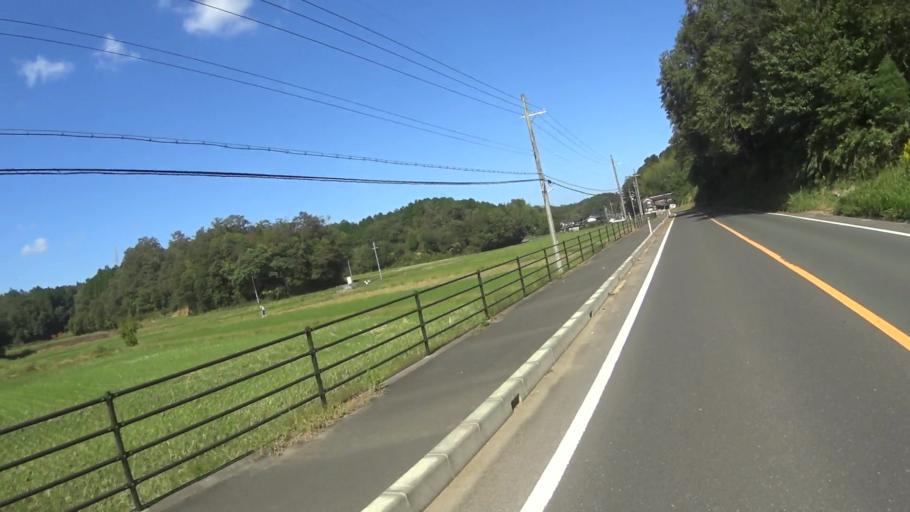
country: JP
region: Kyoto
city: Miyazu
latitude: 35.6495
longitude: 135.0687
